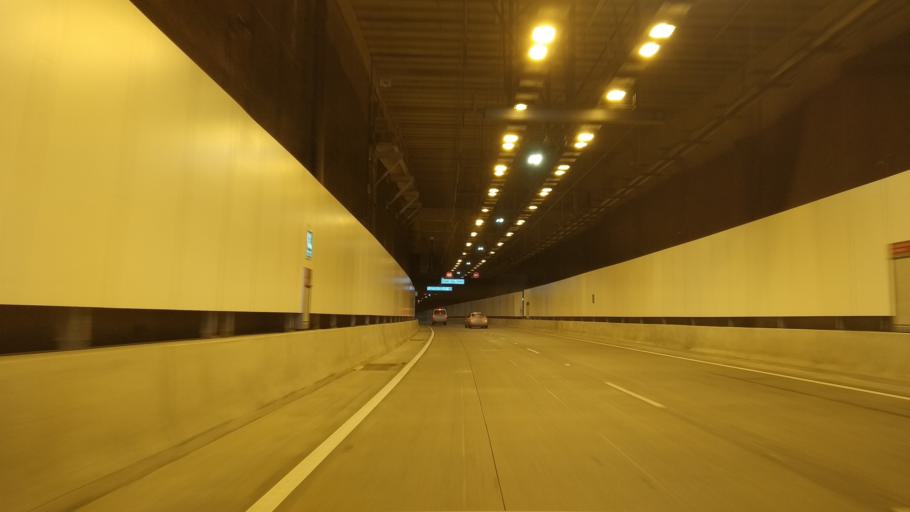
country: AU
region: New South Wales
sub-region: Ashfield
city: Summer Hill
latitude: -33.8817
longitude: 151.1324
